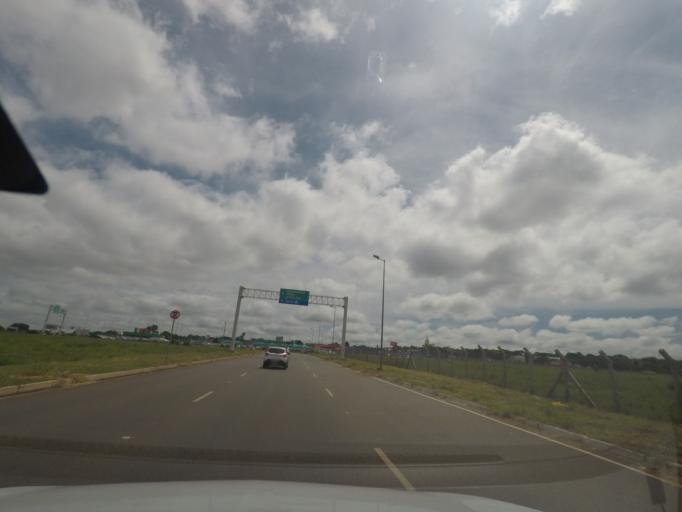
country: BR
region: Goias
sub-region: Goiania
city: Goiania
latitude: -16.6302
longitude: -49.2087
